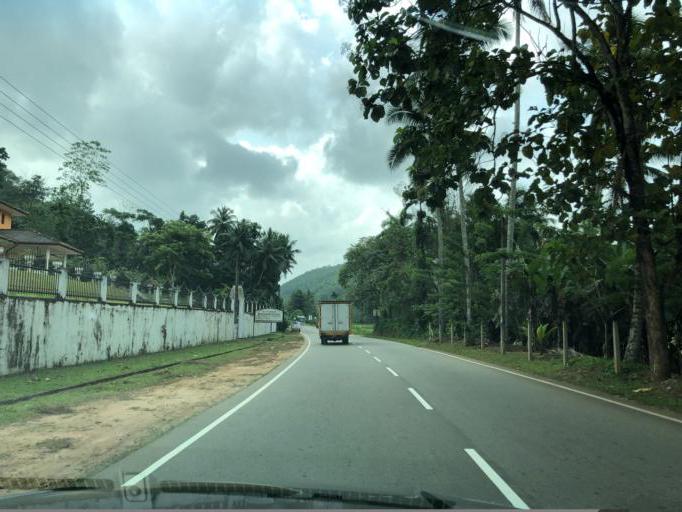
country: LK
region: Western
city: Horana South
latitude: 6.6872
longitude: 80.1442
